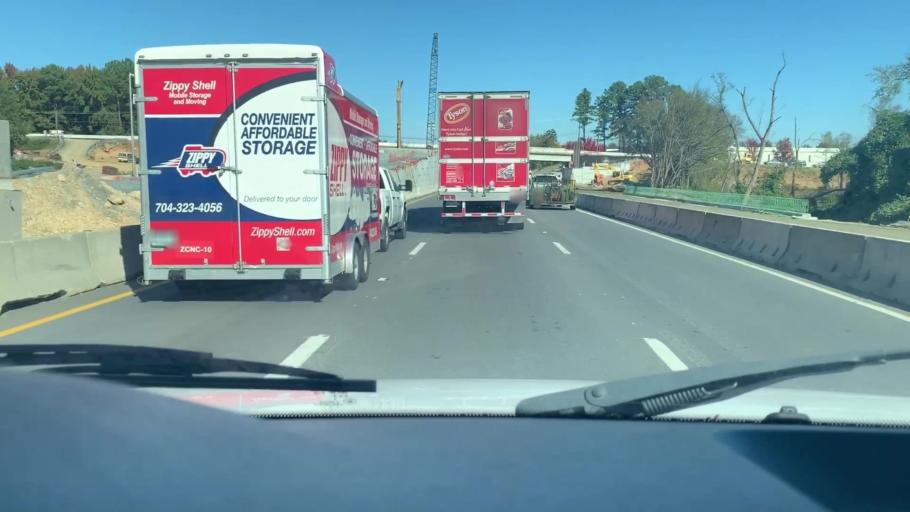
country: US
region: North Carolina
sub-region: Mecklenburg County
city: Huntersville
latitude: 35.3322
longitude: -80.8482
